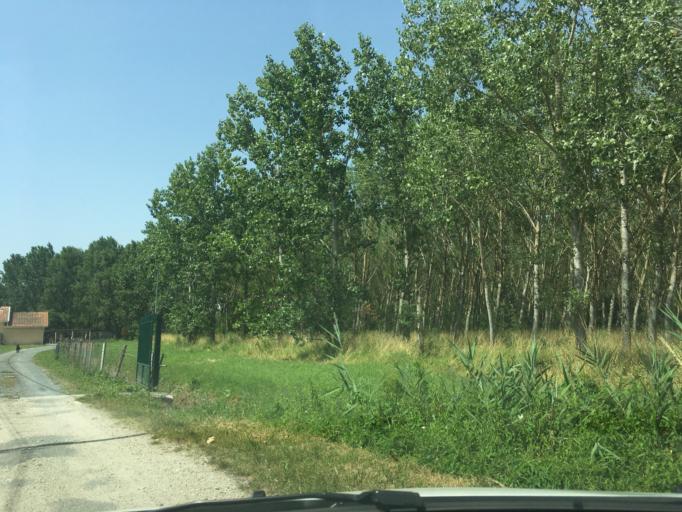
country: FR
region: Aquitaine
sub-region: Departement de la Gironde
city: Cantenac
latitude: 45.0261
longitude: -0.6390
